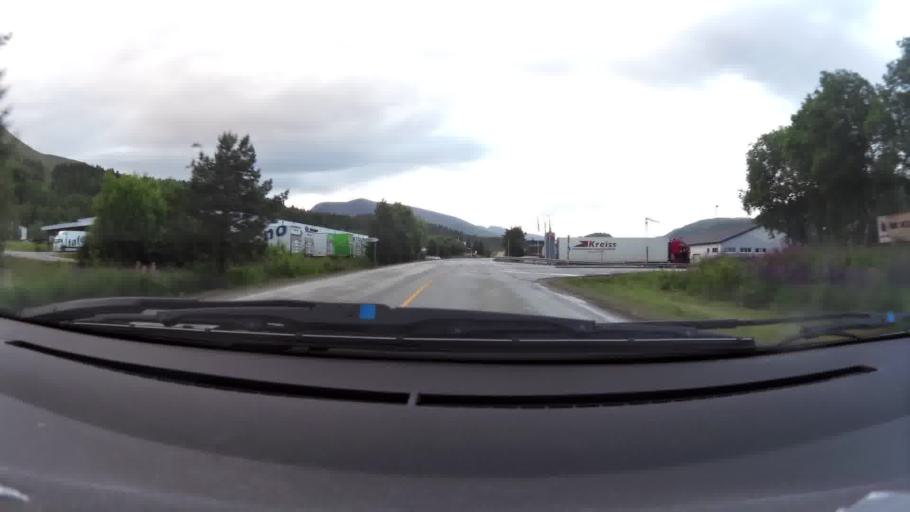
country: NO
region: More og Romsdal
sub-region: Molde
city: Molde
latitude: 62.7676
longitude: 7.2782
